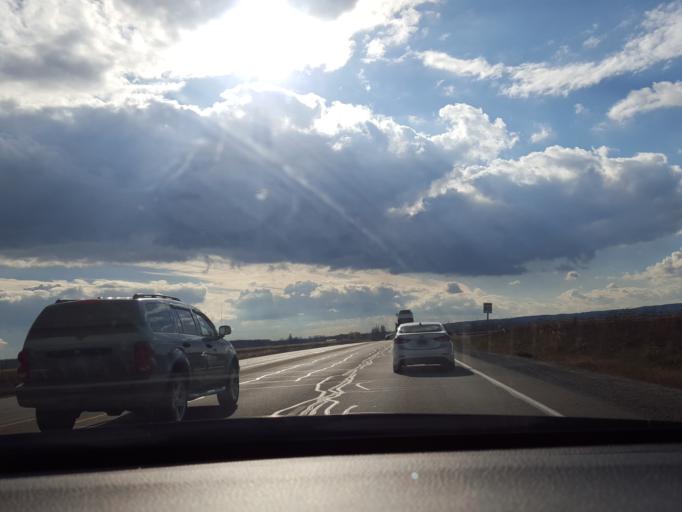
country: CA
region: Ontario
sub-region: Halton
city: Milton
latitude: 43.5622
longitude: -79.8005
